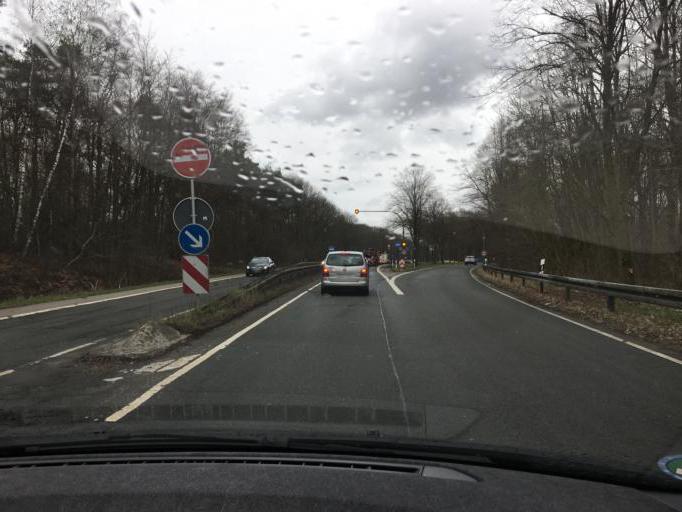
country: DE
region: North Rhine-Westphalia
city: Herdecke
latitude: 51.4360
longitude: 7.4736
